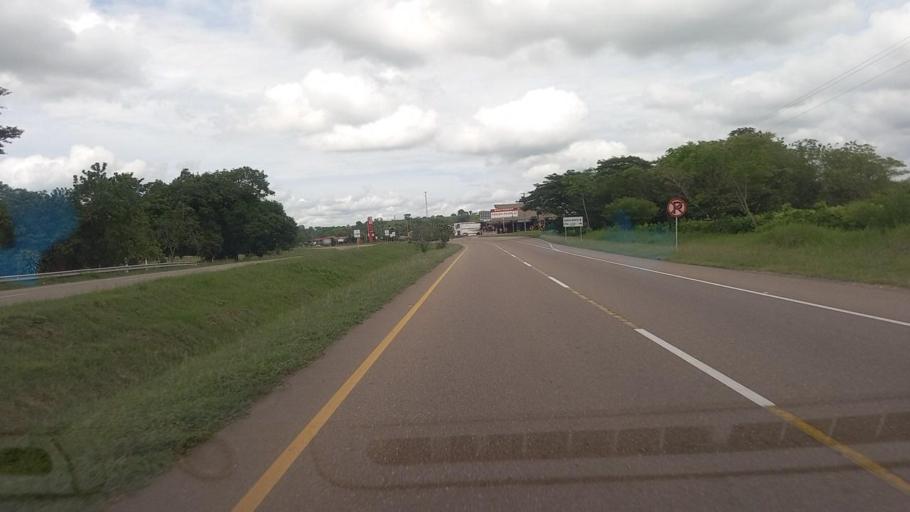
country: CO
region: Antioquia
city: Puerto Triunfo
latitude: 5.7501
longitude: -74.6275
